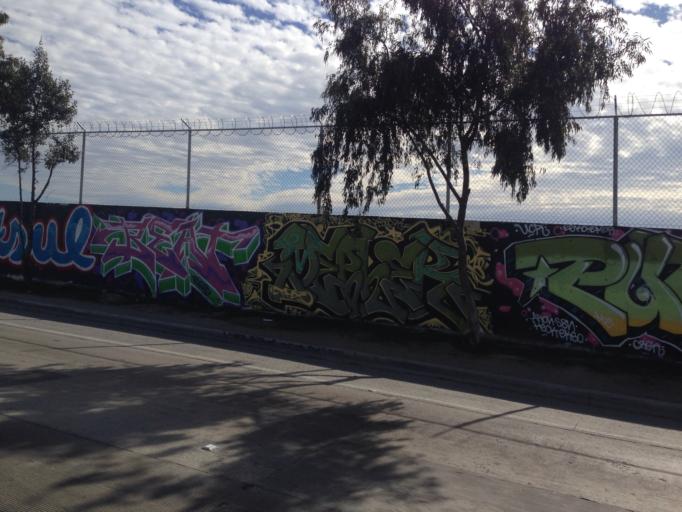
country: MX
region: Baja California
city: Tijuana
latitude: 32.5451
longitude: -116.9969
